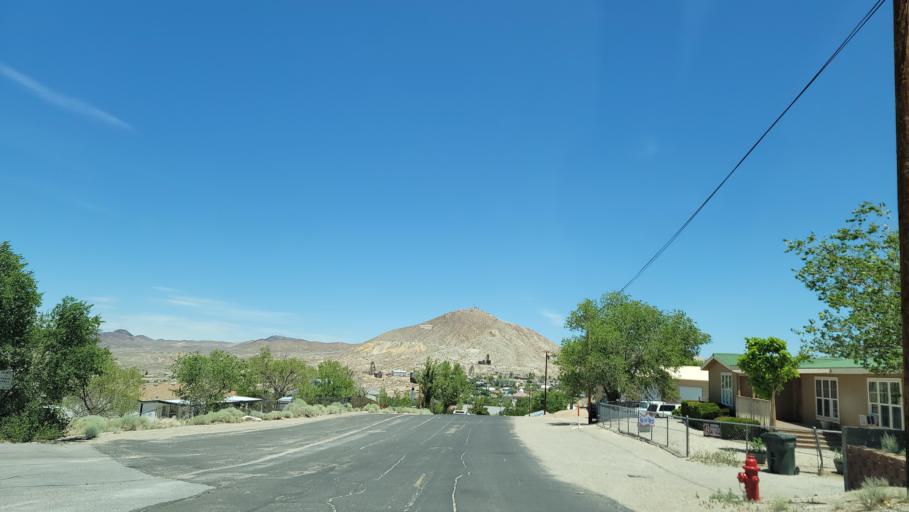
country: US
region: Nevada
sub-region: Nye County
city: Tonopah
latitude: 38.0607
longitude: -117.2317
